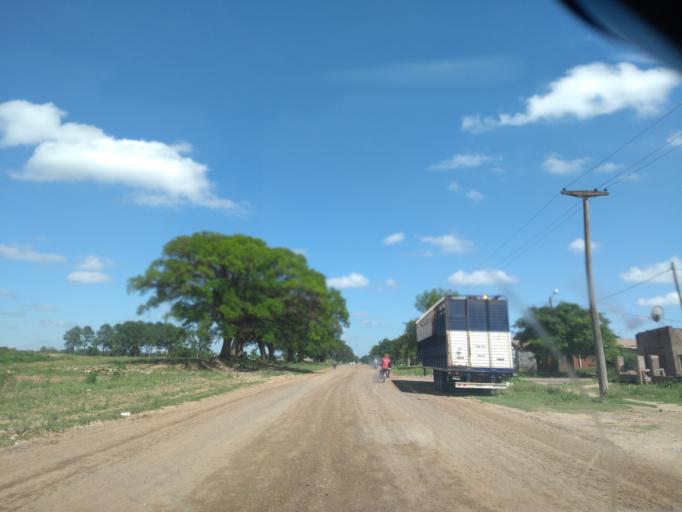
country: AR
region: Chaco
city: Fontana
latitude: -27.4082
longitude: -59.0348
